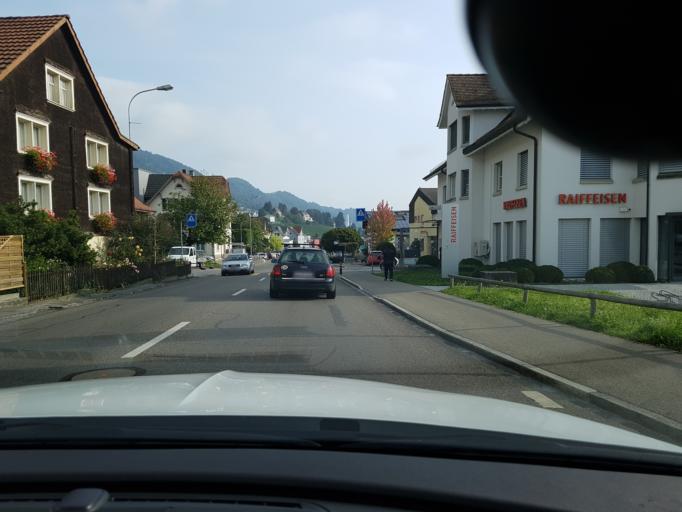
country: CH
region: Saint Gallen
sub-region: Wahlkreis Rheintal
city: Rebstein
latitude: 47.3921
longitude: 9.5691
